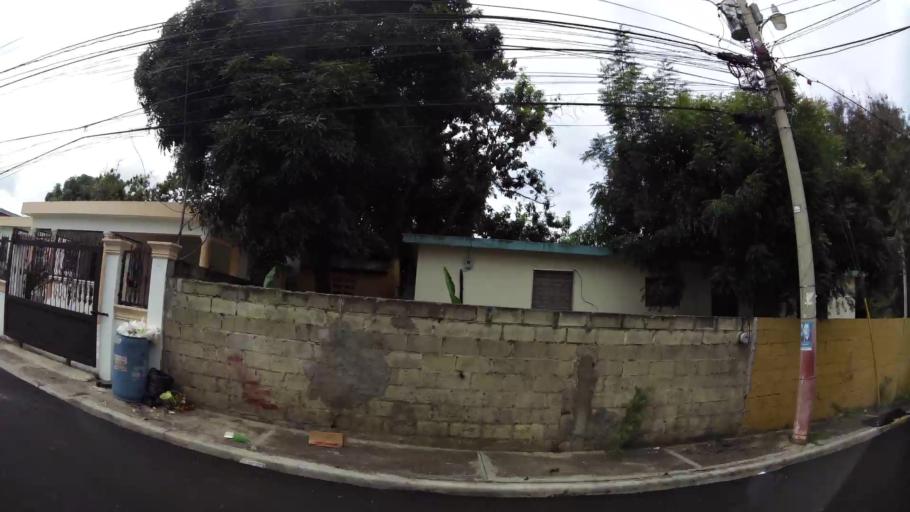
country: DO
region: Santiago
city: Santiago de los Caballeros
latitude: 19.4406
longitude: -70.6693
